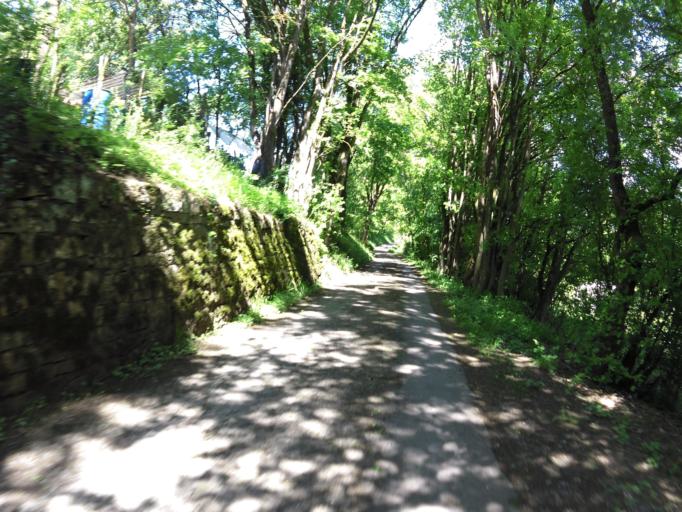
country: DE
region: Bavaria
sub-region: Regierungsbezirk Unterfranken
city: Reichenberg
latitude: 49.7493
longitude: 9.9344
